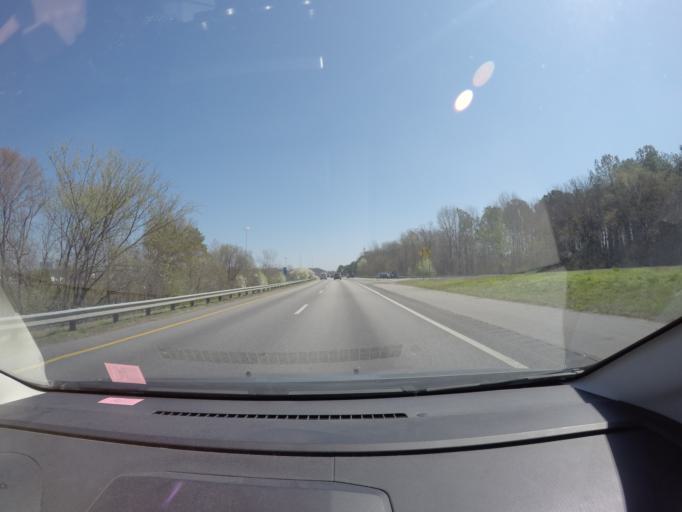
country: US
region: Tennessee
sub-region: Hamilton County
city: East Ridge
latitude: 35.0049
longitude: -85.2099
